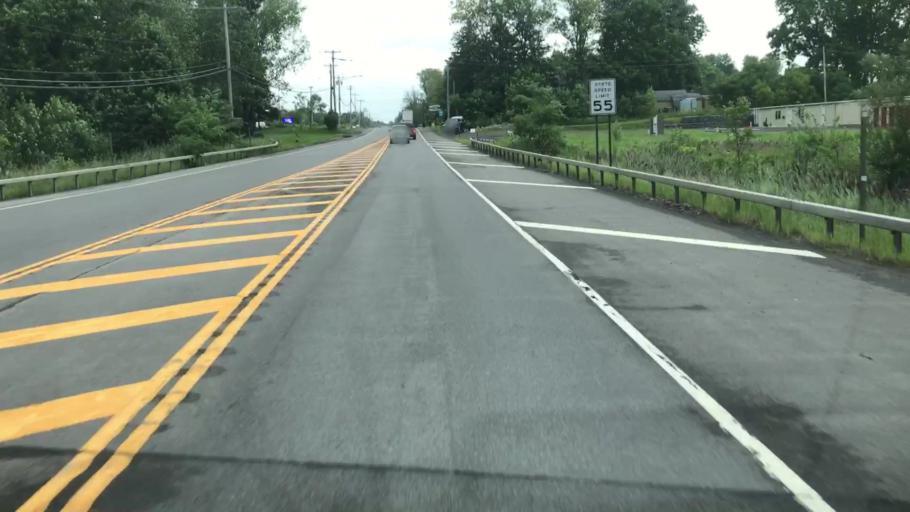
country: US
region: New York
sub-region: Onondaga County
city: Liverpool
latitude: 43.1862
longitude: -76.2134
